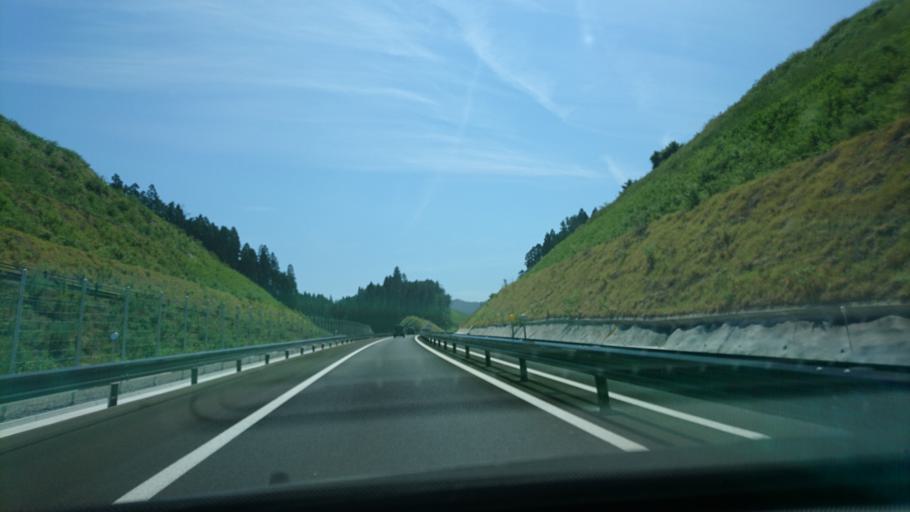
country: JP
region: Iwate
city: Ofunato
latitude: 39.0003
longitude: 141.6148
